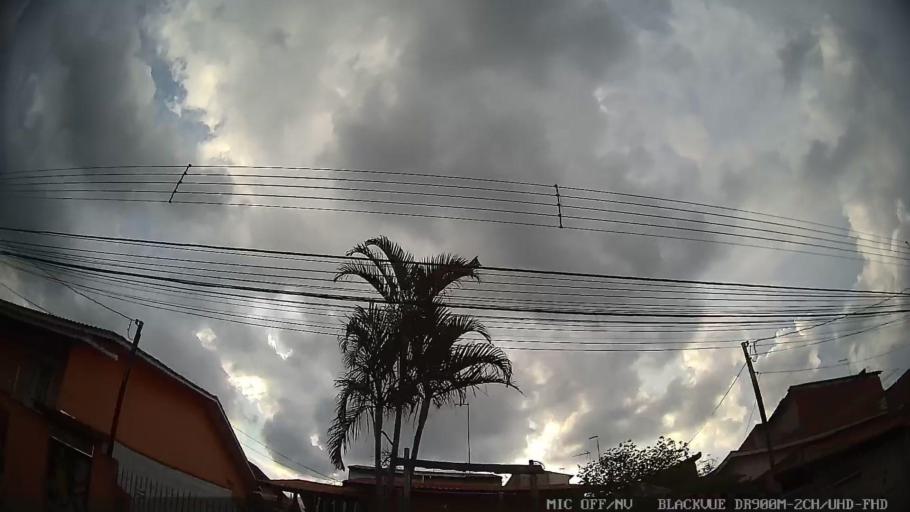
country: BR
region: Sao Paulo
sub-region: Braganca Paulista
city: Braganca Paulista
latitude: -22.9170
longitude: -46.5266
